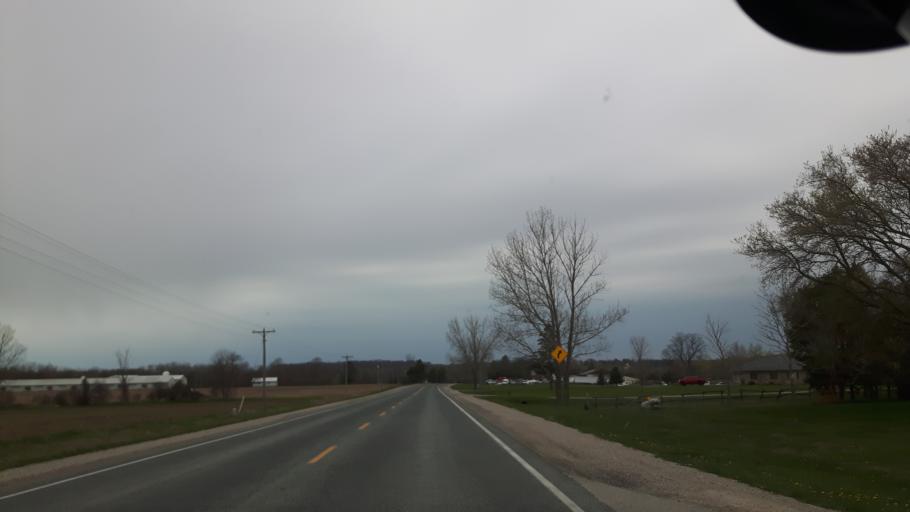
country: CA
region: Ontario
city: Bluewater
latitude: 43.6367
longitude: -81.5849
